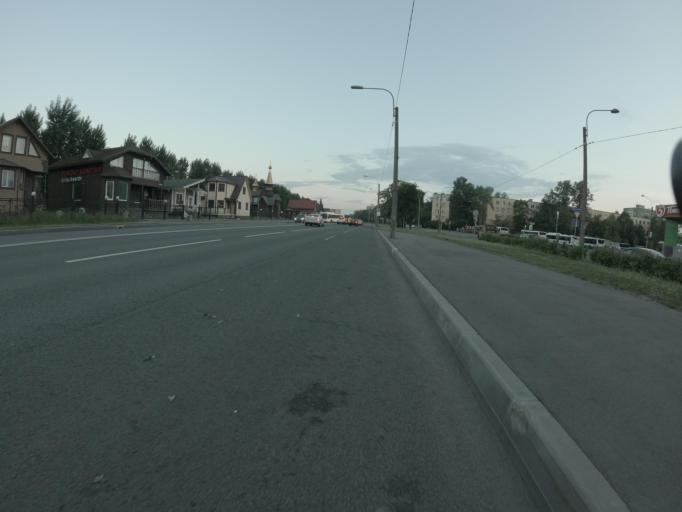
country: RU
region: St.-Petersburg
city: Dachnoye
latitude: 59.8438
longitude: 30.2775
